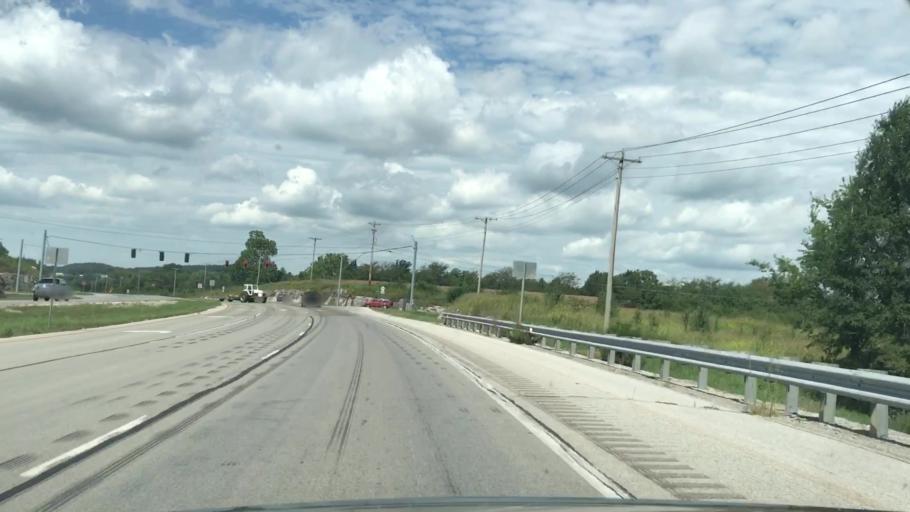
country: US
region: Kentucky
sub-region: Logan County
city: Russellville
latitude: 36.8649
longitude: -86.8668
